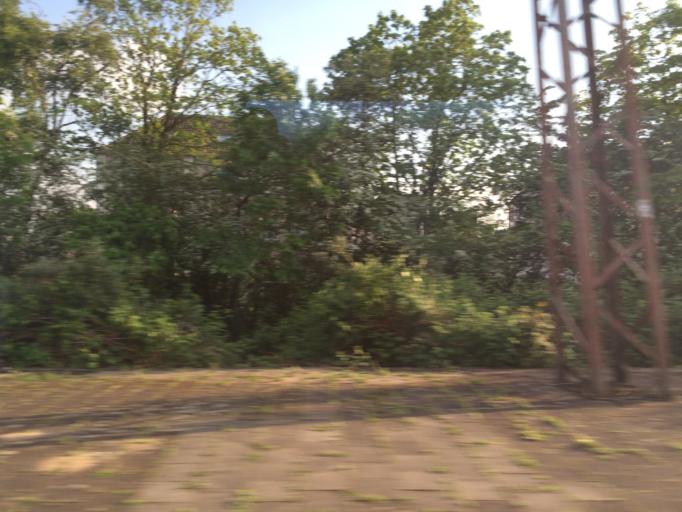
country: DE
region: North Rhine-Westphalia
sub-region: Regierungsbezirk Dusseldorf
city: Muelheim (Ruhr)
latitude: 51.4484
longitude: 6.8546
